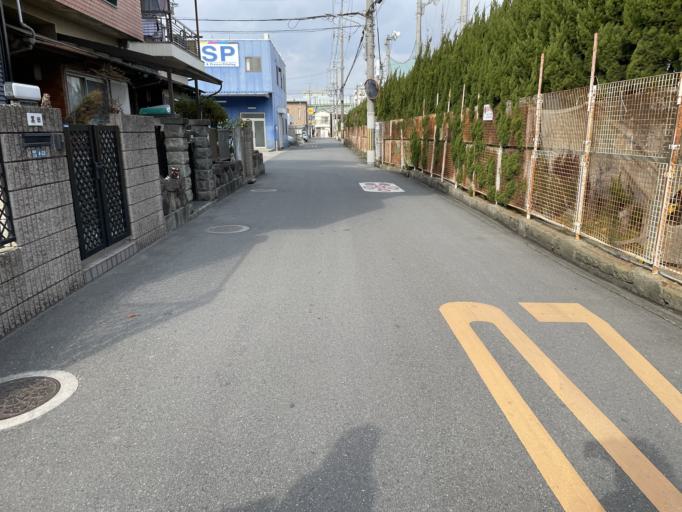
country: JP
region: Osaka
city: Daitocho
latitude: 34.6765
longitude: 135.5807
